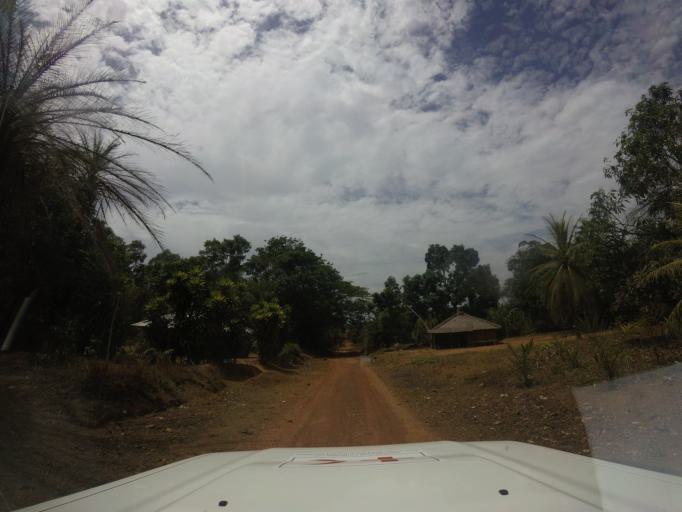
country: SL
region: Southern Province
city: Zimmi
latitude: 7.1030
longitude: -11.2751
